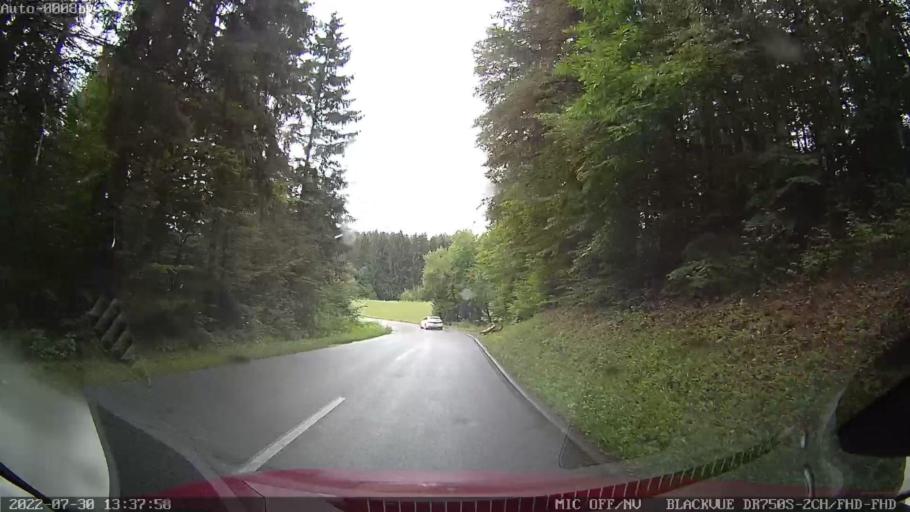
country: SI
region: Zuzemberk
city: Zuzemberk
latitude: 45.8812
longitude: 14.9137
